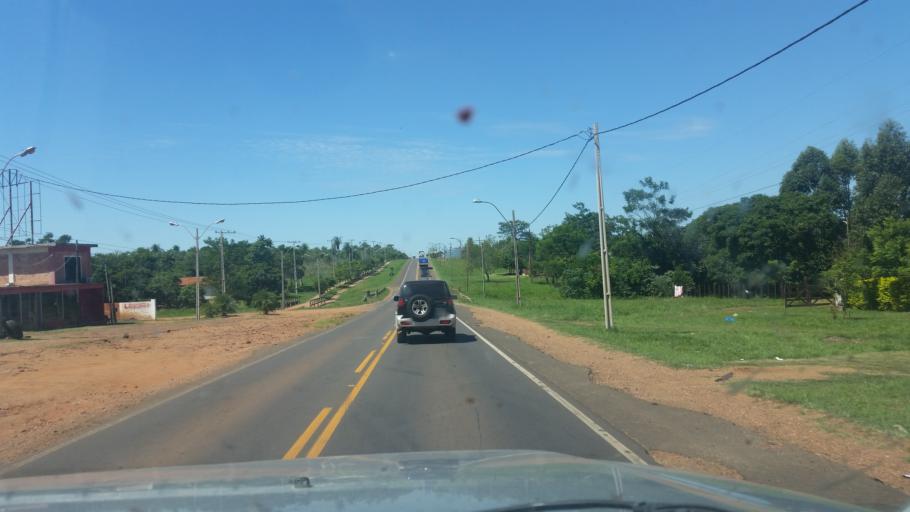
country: PY
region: Misiones
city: San Juan Bautista
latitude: -26.6723
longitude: -57.1260
